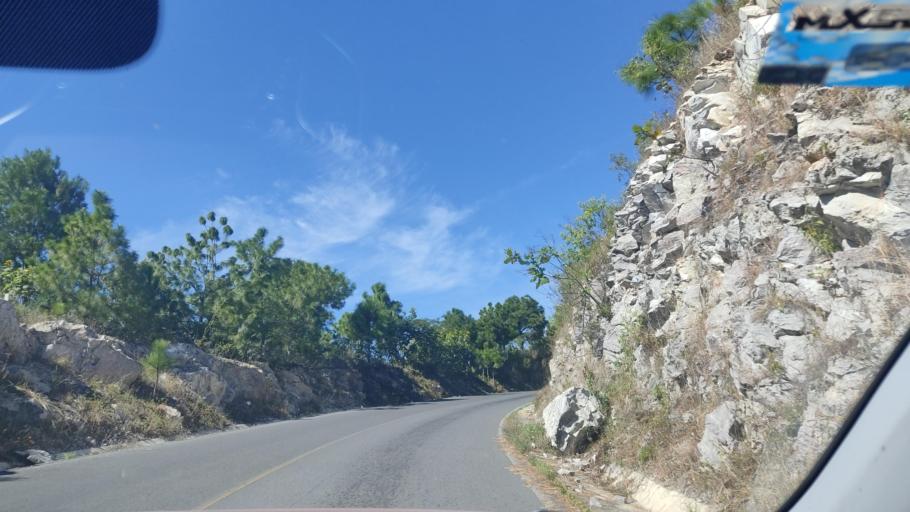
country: MX
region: Nayarit
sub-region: Jala
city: Rosa Blanca
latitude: 21.1001
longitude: -104.3637
